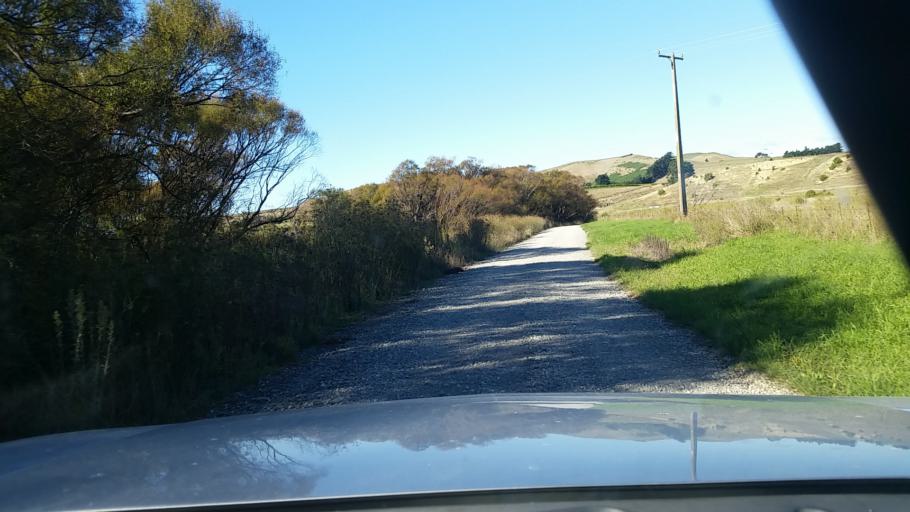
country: NZ
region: Marlborough
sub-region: Marlborough District
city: Blenheim
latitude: -41.6780
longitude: 174.1373
